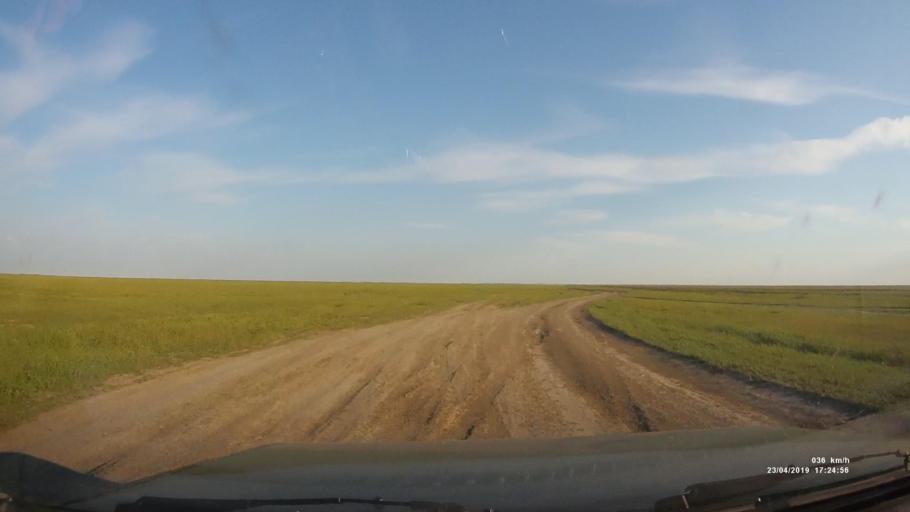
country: RU
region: Kalmykiya
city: Priyutnoye
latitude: 46.1549
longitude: 43.5094
